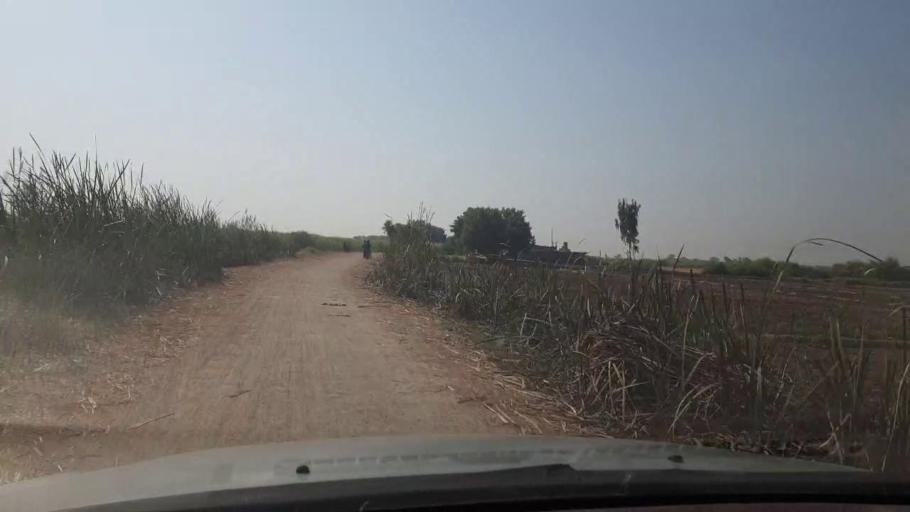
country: PK
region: Sindh
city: Bulri
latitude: 24.9110
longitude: 68.4348
